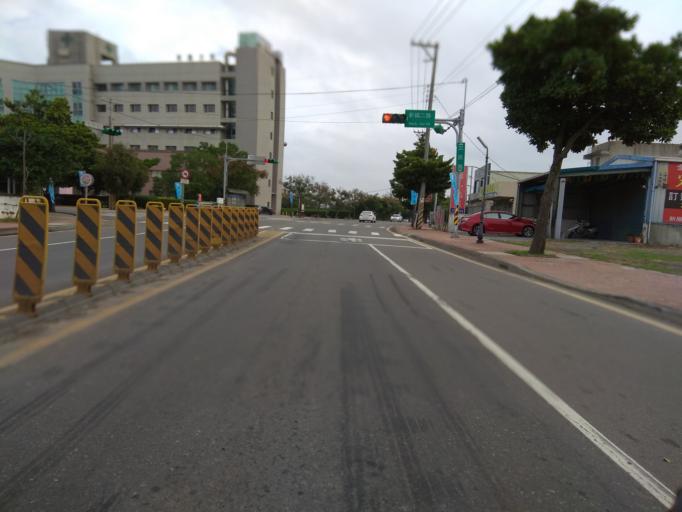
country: TW
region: Taiwan
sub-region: Hsinchu
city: Zhubei
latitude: 24.9686
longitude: 121.1067
